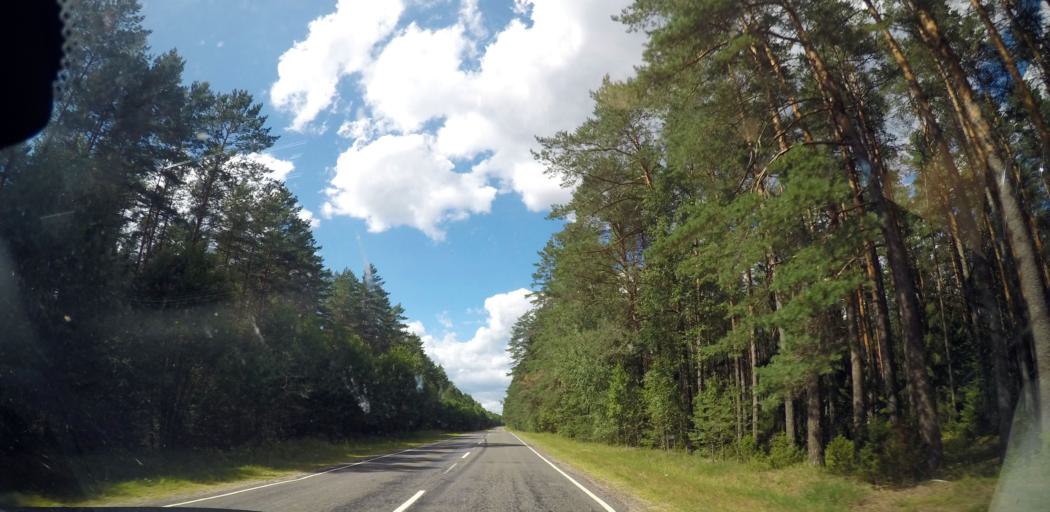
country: BY
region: Grodnenskaya
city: Skidal'
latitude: 53.8483
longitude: 24.2005
